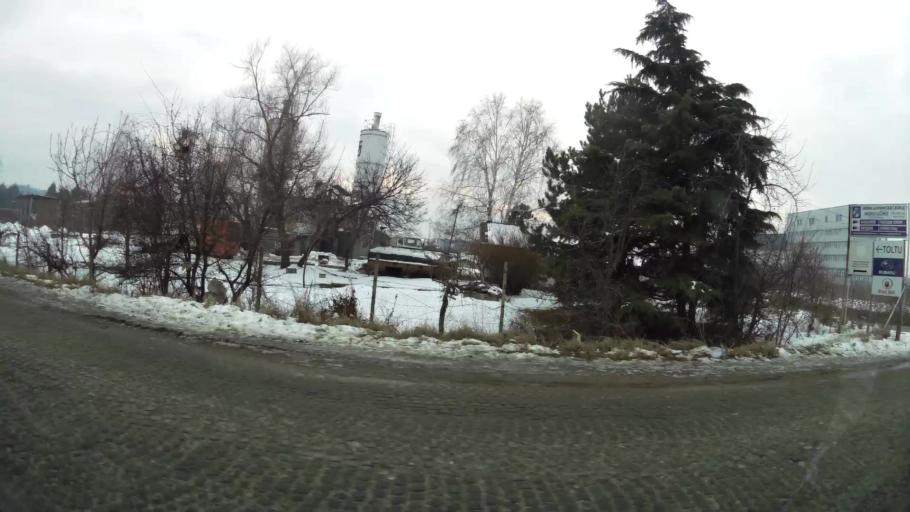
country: MK
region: Suto Orizari
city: Suto Orizare
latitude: 42.0481
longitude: 21.4288
